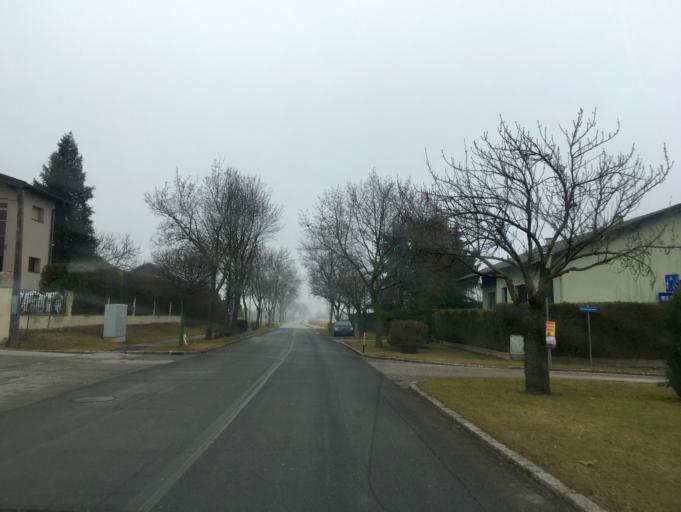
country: AT
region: Lower Austria
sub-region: Politischer Bezirk Bruck an der Leitha
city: Trautmannsdorf an der Leitha
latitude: 48.0521
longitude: 16.6487
